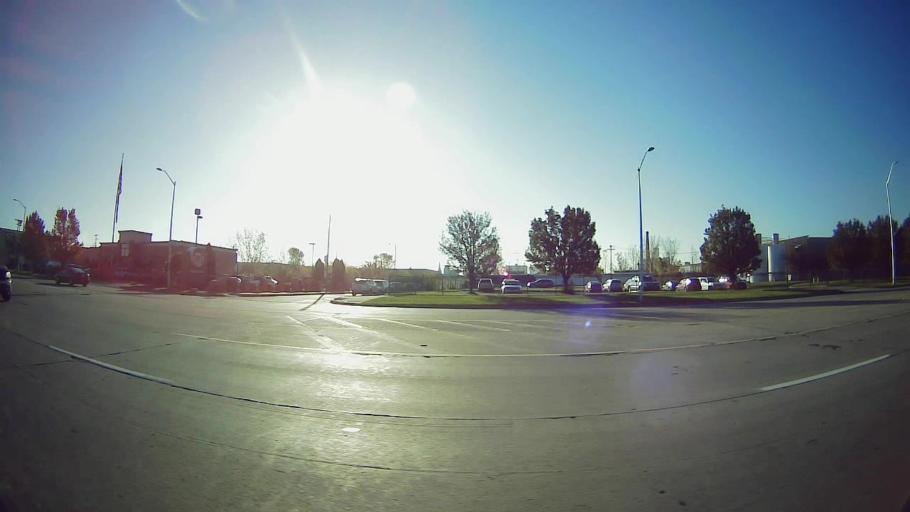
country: US
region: Michigan
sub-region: Wayne County
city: Detroit
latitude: 42.3538
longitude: -83.0424
